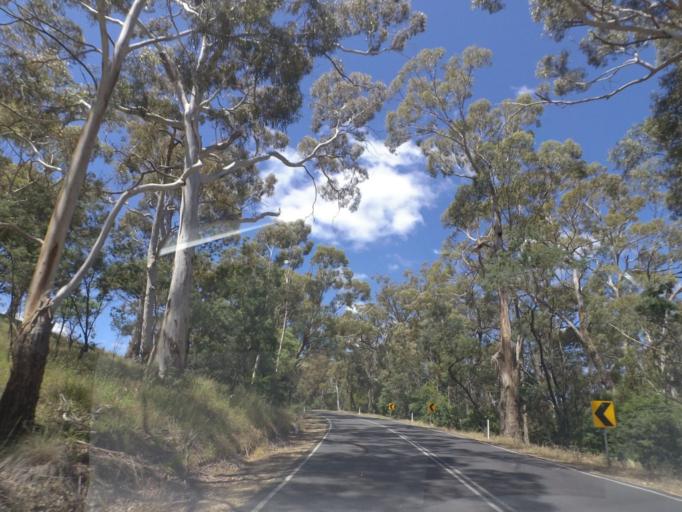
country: AU
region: Victoria
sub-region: Mount Alexander
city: Castlemaine
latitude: -37.2904
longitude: 144.2663
